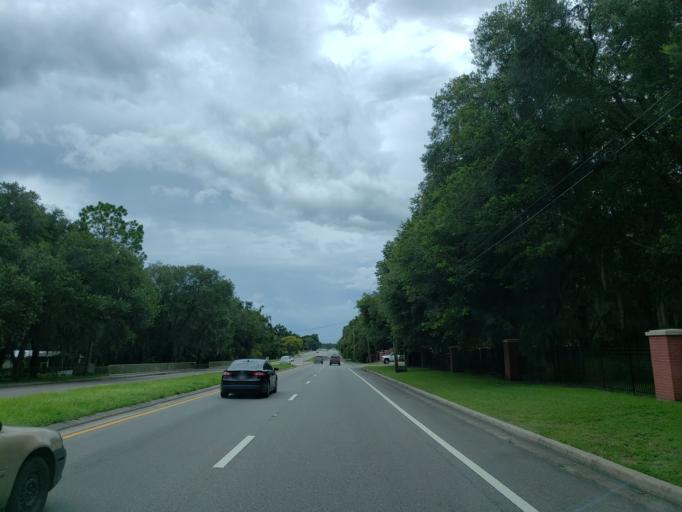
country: US
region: Florida
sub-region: Polk County
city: Willow Oak
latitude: 27.9377
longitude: -82.0554
